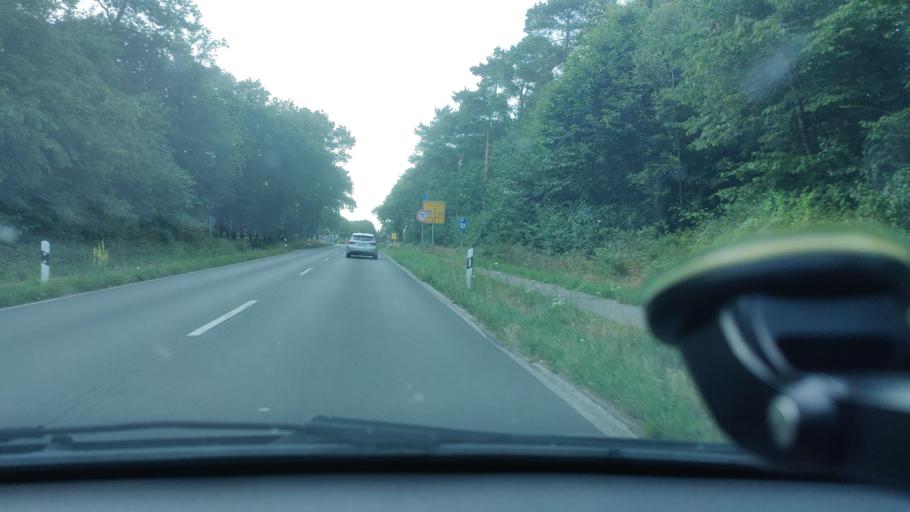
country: DE
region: North Rhine-Westphalia
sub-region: Regierungsbezirk Dusseldorf
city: Alpen
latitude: 51.5646
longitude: 6.4961
